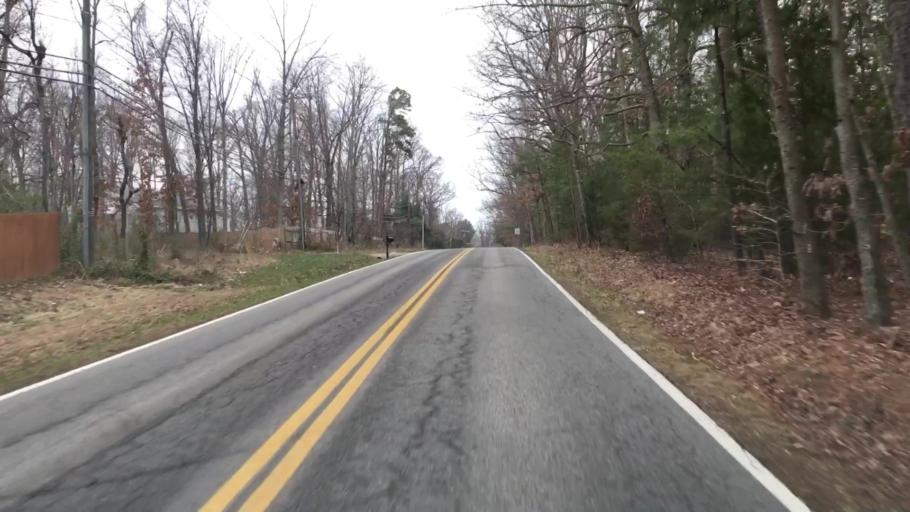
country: US
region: Virginia
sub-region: Chesterfield County
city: Bon Air
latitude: 37.5161
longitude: -77.5755
